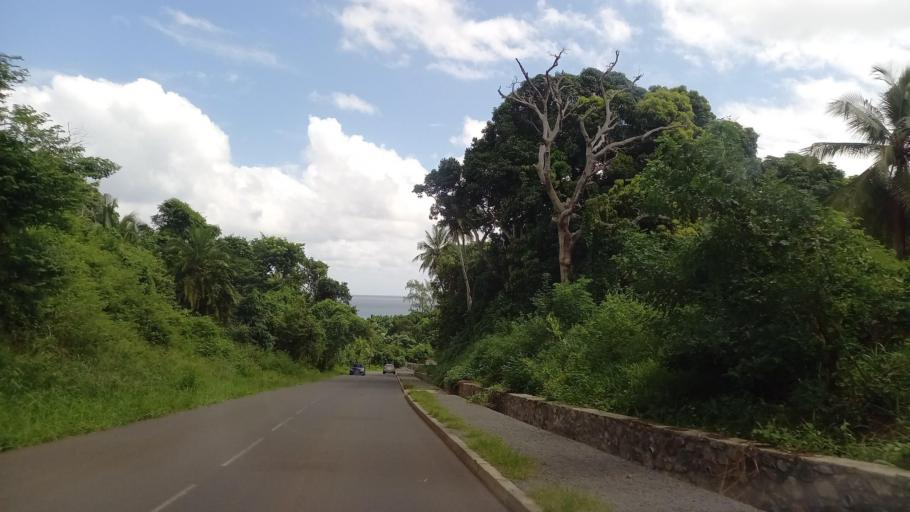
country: YT
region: Boueni
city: Boueni
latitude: -12.9248
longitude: 45.0930
